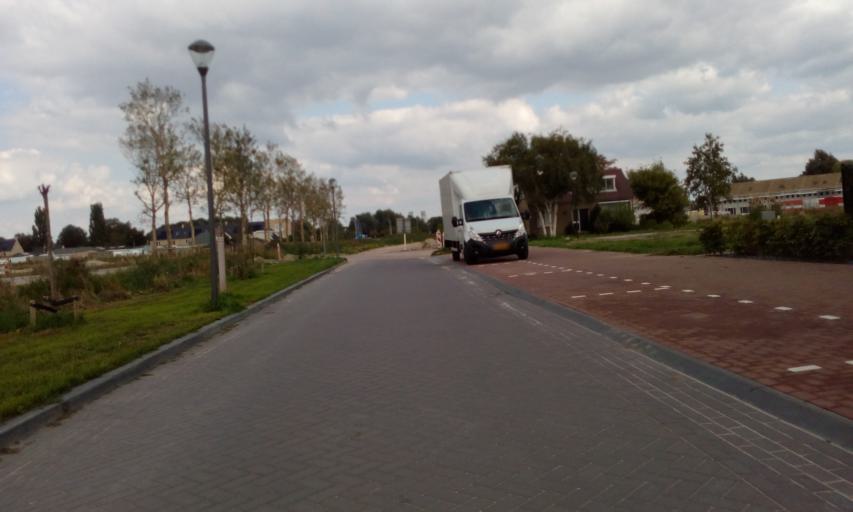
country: NL
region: South Holland
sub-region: Gemeente Waddinxveen
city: Waddinxveen
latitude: 52.0348
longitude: 4.6452
